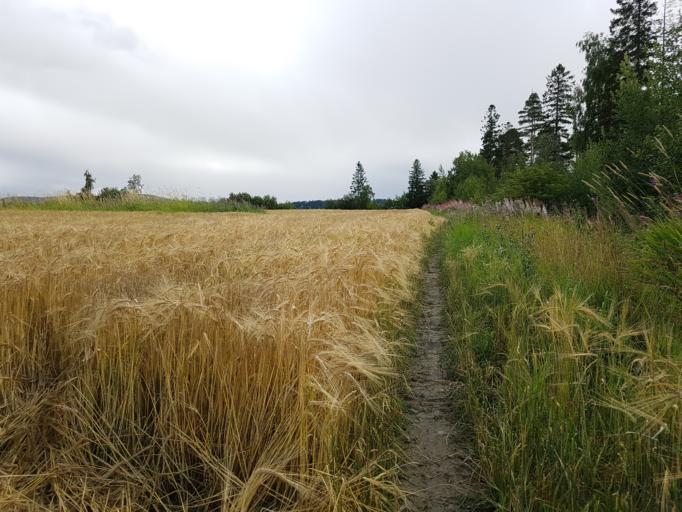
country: NO
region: Sor-Trondelag
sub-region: Trondheim
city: Trondheim
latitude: 63.4235
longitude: 10.4779
